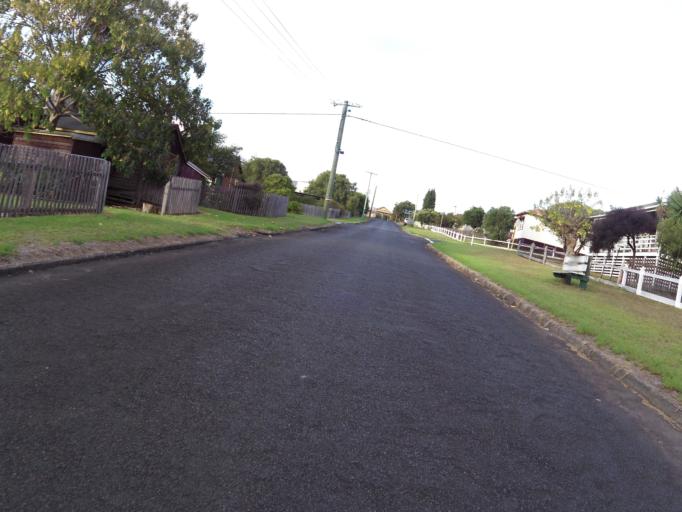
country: AU
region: Western Australia
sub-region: Manjimup
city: Pemberton
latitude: -34.4477
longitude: 116.0331
